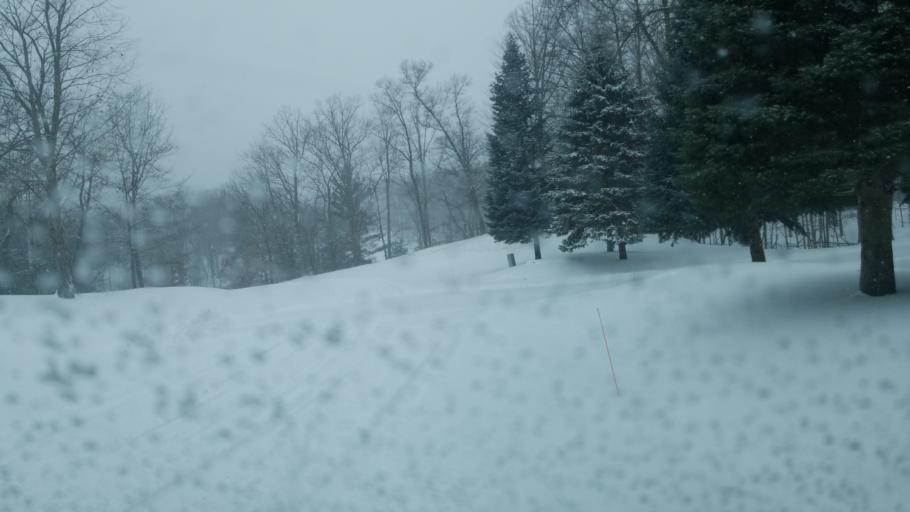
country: US
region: Michigan
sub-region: Mecosta County
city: Canadian Lakes
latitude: 43.6110
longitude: -85.3061
